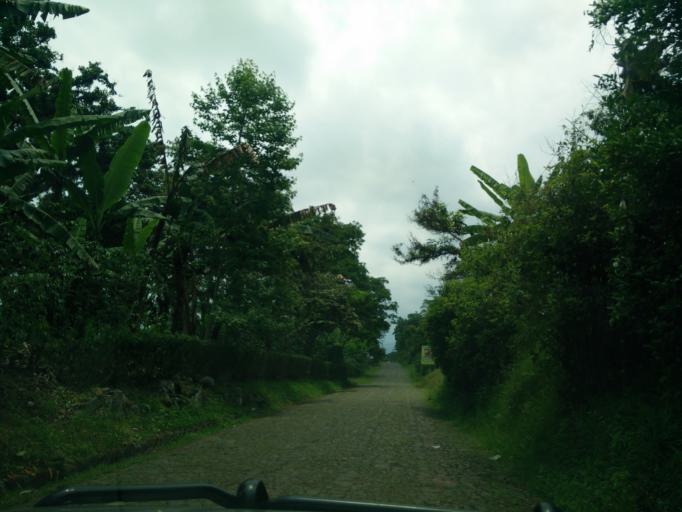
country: MX
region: Veracruz
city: Xico
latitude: 19.4122
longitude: -96.9937
